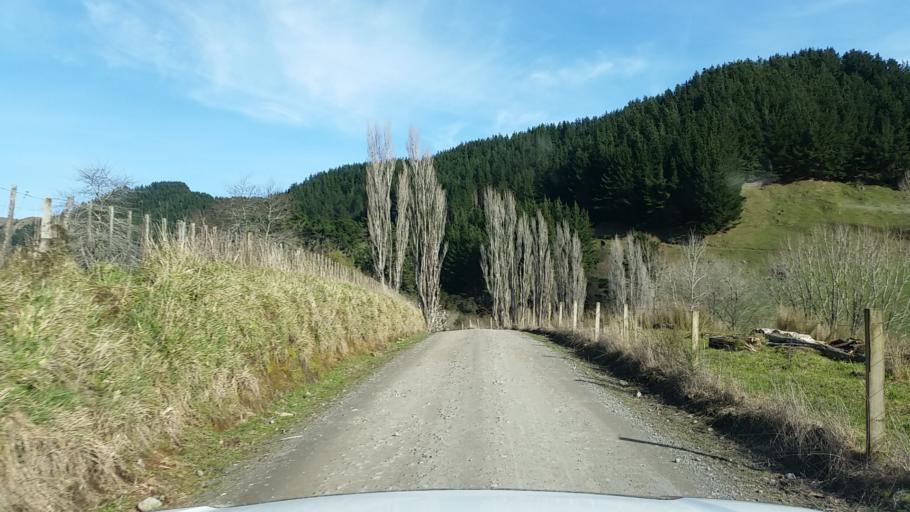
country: NZ
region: Taranaki
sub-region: South Taranaki District
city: Eltham
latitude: -39.3558
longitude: 174.5125
